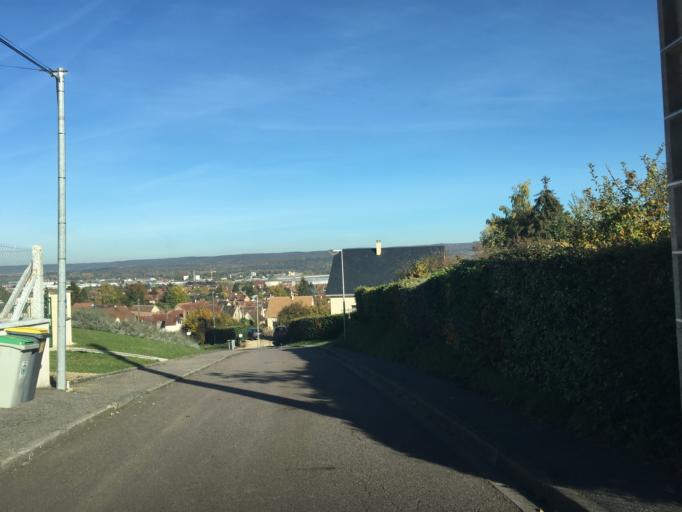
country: FR
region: Haute-Normandie
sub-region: Departement de l'Eure
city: Vernon
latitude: 49.0873
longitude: 1.4577
